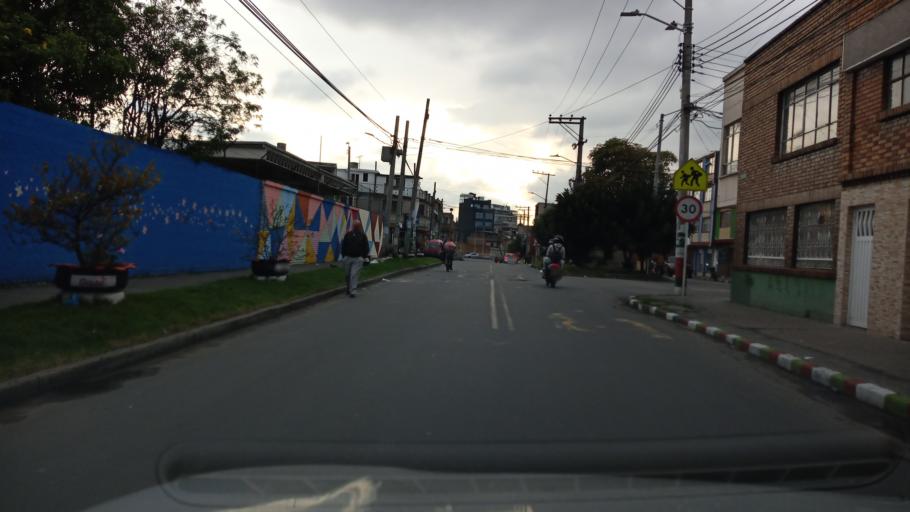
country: CO
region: Bogota D.C.
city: Bogota
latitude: 4.5868
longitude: -74.1132
